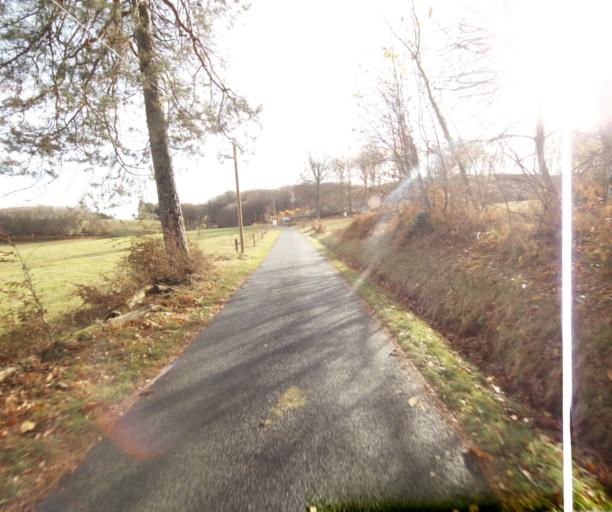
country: FR
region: Limousin
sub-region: Departement de la Correze
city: Cornil
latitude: 45.1914
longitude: 1.7265
